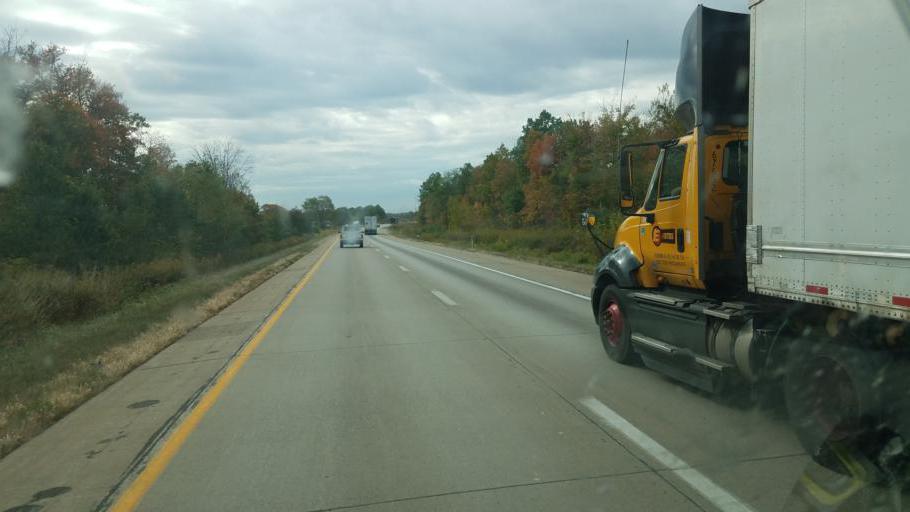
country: US
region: Pennsylvania
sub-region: Lawrence County
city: New Wilmington
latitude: 41.1859
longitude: -80.3575
